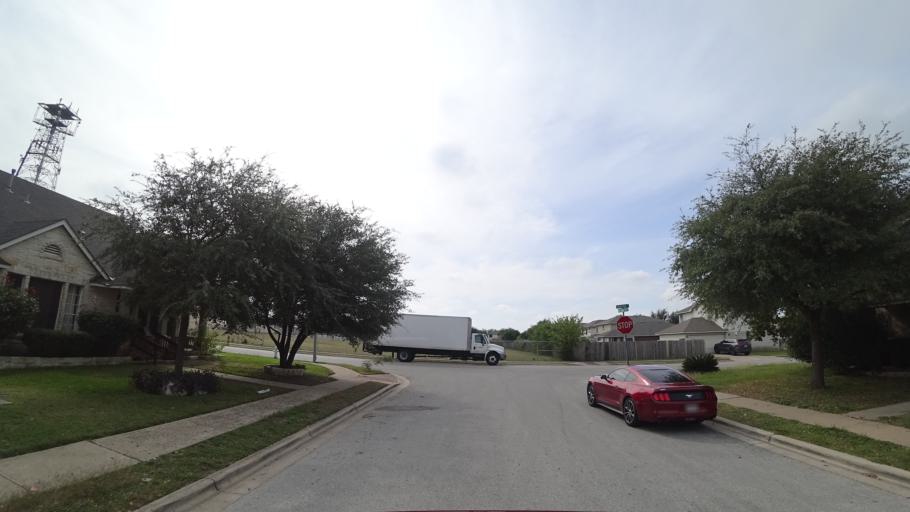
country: US
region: Texas
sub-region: Travis County
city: Windemere
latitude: 30.4452
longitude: -97.6540
